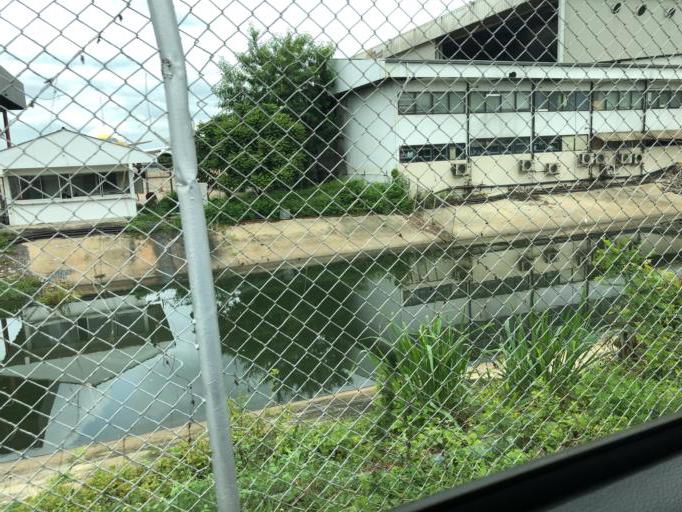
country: TH
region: Bangkok
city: Don Mueang
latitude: 13.9317
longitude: 100.6103
